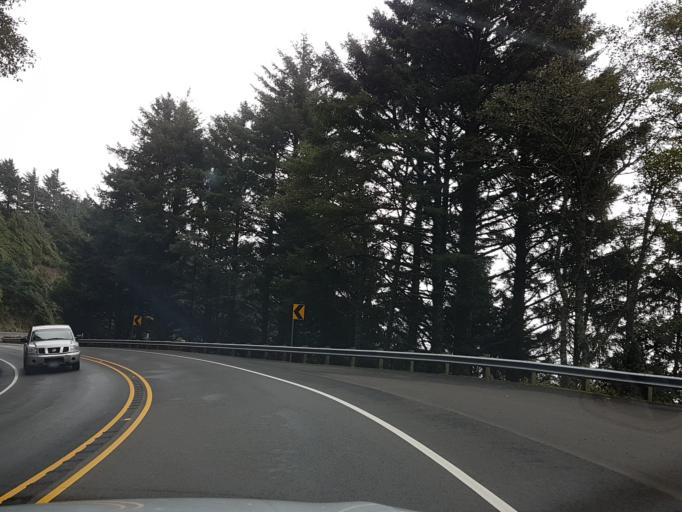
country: US
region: Oregon
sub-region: Lane County
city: Florence
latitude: 44.1156
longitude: -124.1224
